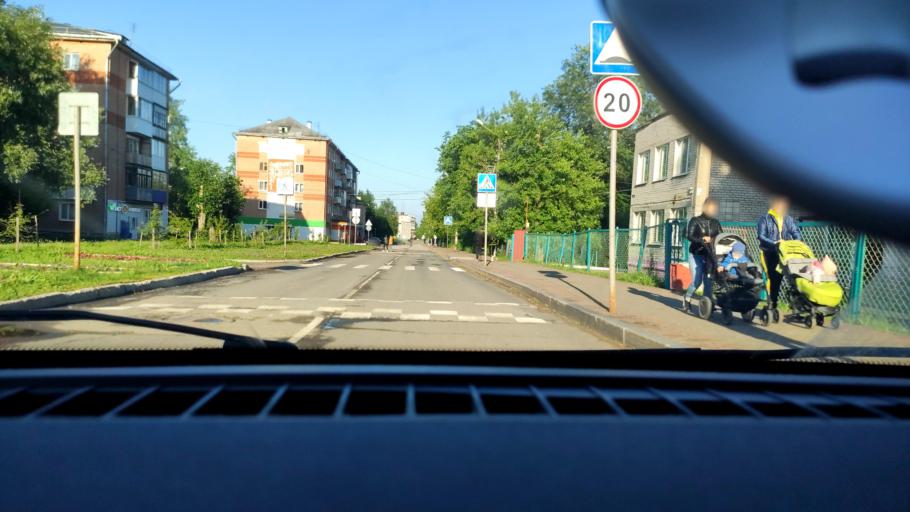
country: RU
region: Perm
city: Novyye Lyady
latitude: 58.0505
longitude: 56.5843
